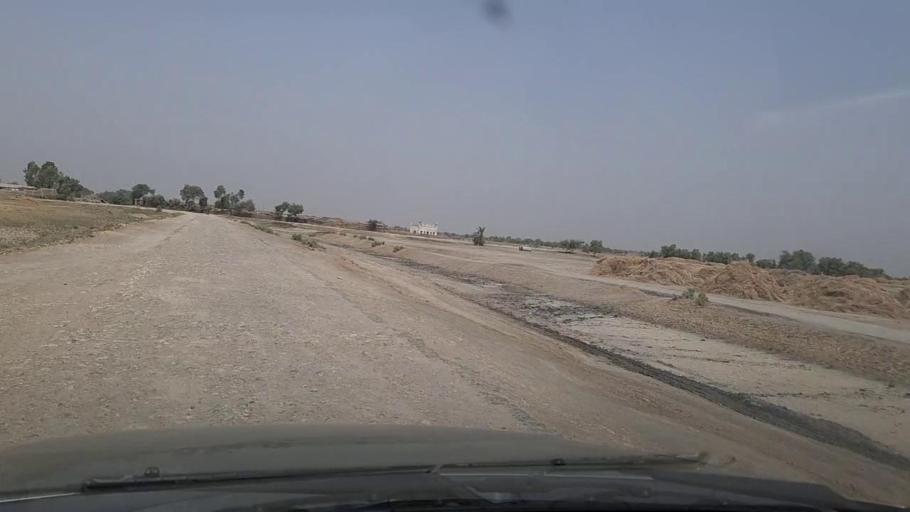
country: PK
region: Balochistan
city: Sohbatpur
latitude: 28.4149
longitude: 68.6899
